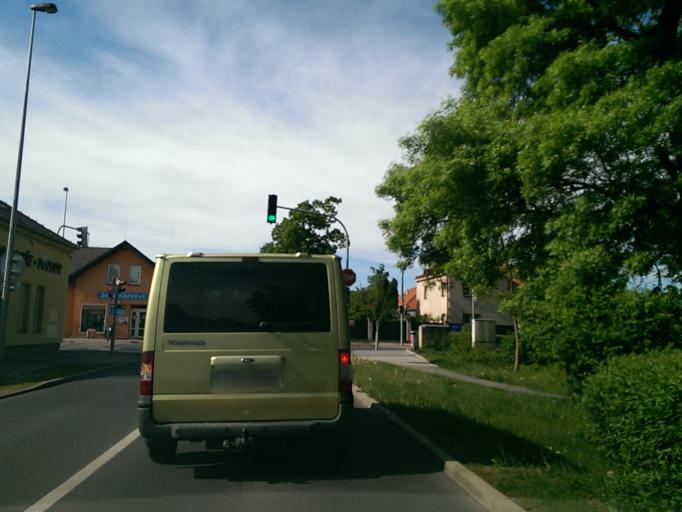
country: CZ
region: Praha
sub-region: Praha 20
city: Horni Pocernice
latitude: 50.1172
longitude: 14.6258
